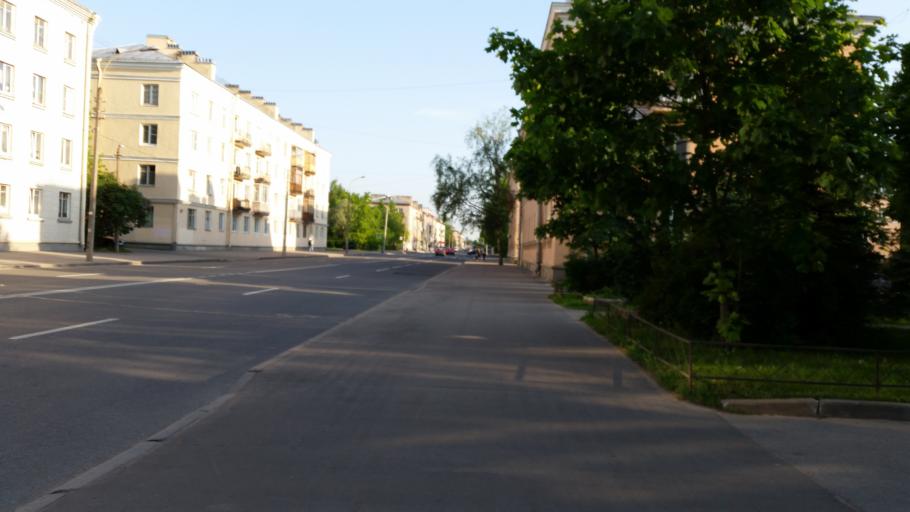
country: RU
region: St.-Petersburg
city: Sosnovaya Polyana
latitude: 59.8428
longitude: 30.1468
